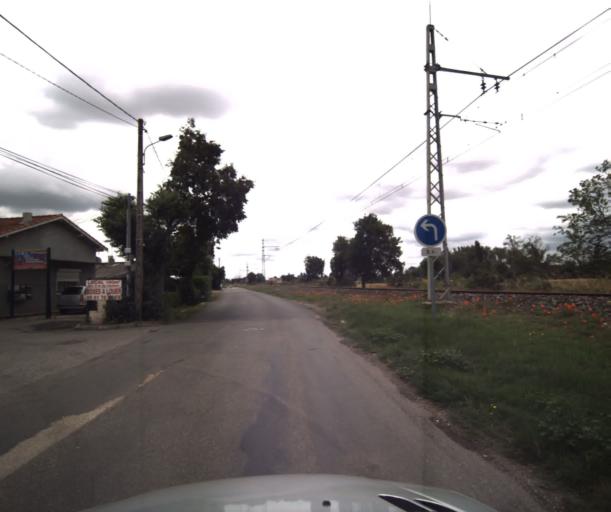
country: FR
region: Midi-Pyrenees
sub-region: Departement de la Haute-Garonne
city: Lacroix-Falgarde
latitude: 43.4916
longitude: 1.3941
